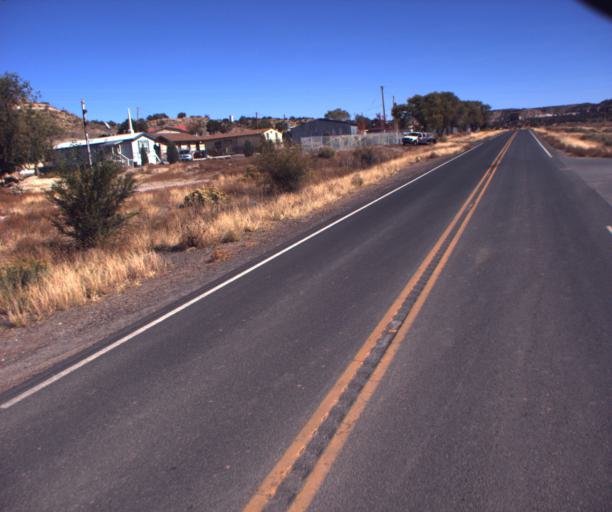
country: US
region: Arizona
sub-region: Apache County
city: Ganado
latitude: 35.7467
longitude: -109.8591
